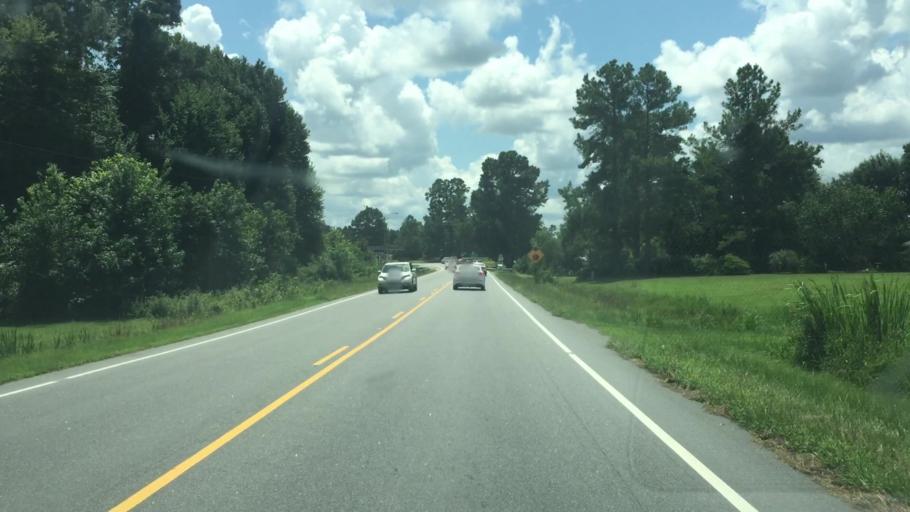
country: US
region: North Carolina
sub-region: Columbus County
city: Tabor City
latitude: 34.1631
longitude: -78.8458
